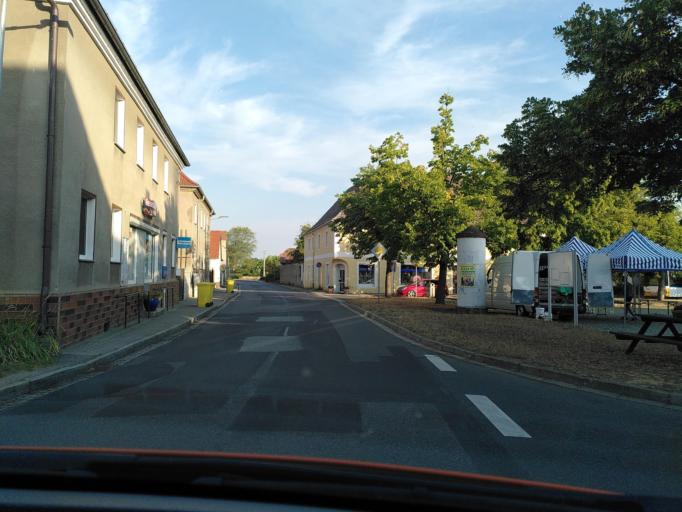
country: DE
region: Saxony
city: Konigswartha
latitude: 51.3097
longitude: 14.3261
